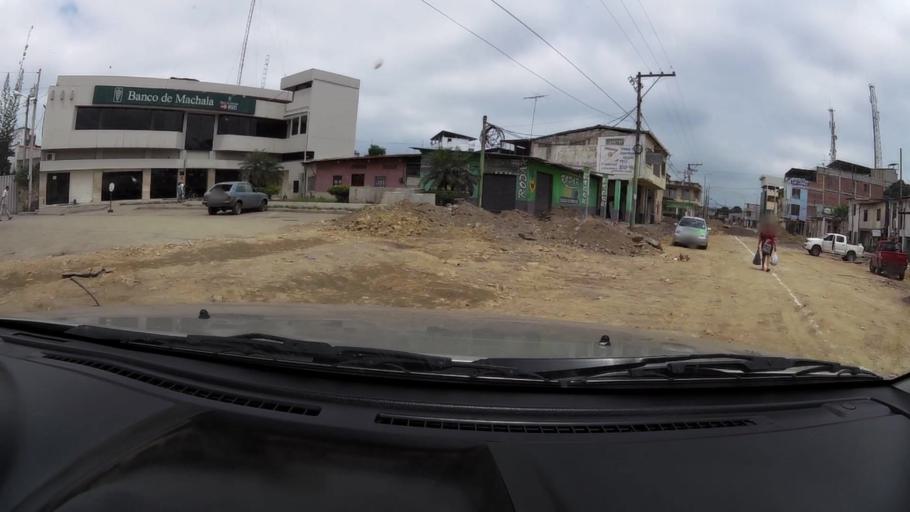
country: EC
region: El Oro
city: Pasaje
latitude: -3.2470
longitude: -79.8330
